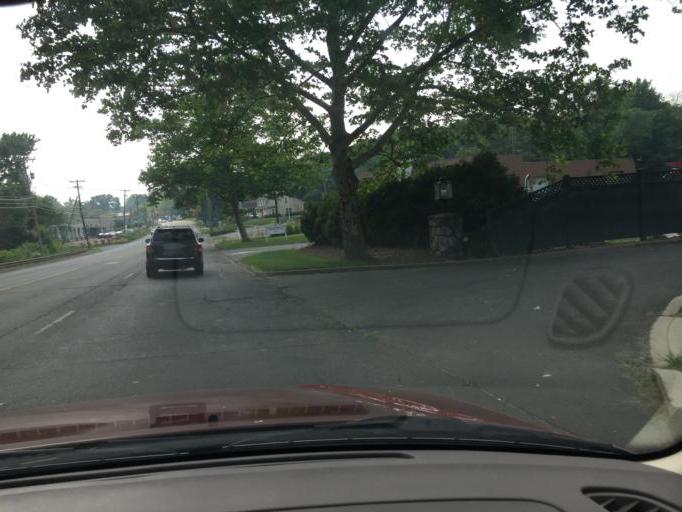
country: US
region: Connecticut
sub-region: Fairfield County
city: Westport
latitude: 41.1390
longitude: -73.3241
